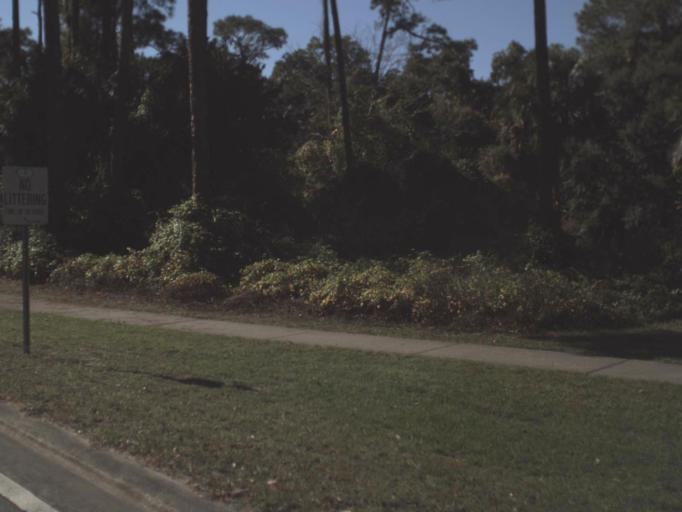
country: US
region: Florida
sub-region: Flagler County
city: Palm Coast
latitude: 29.5655
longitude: -81.1921
